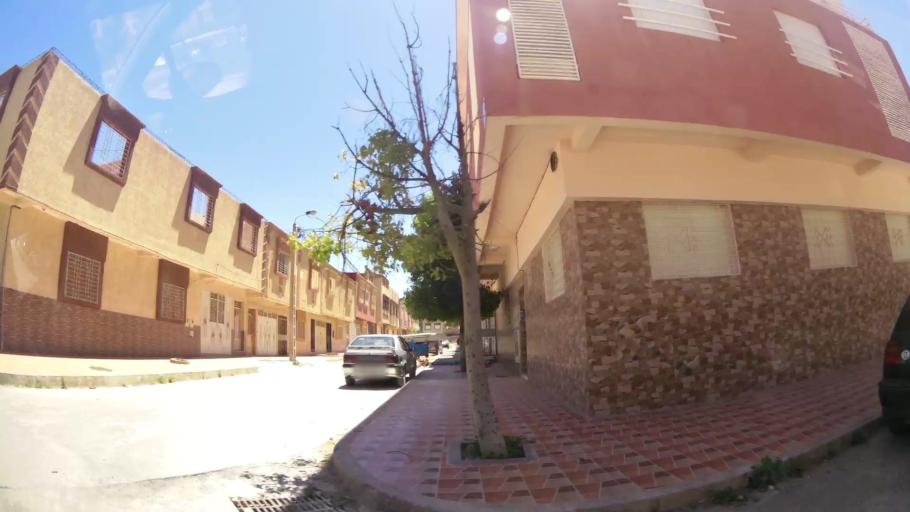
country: MA
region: Oriental
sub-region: Oujda-Angad
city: Oujda
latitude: 34.6771
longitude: -1.8620
